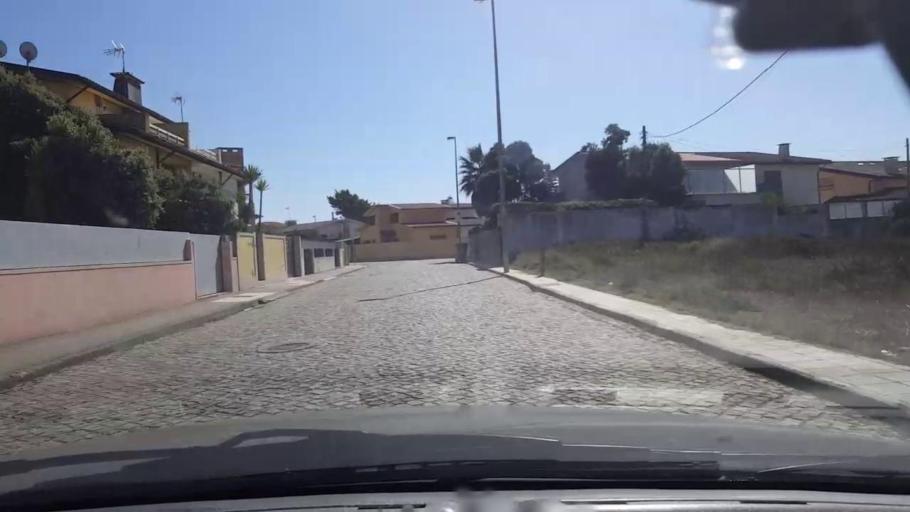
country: PT
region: Porto
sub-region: Vila do Conde
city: Arvore
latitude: 41.3061
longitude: -8.7364
